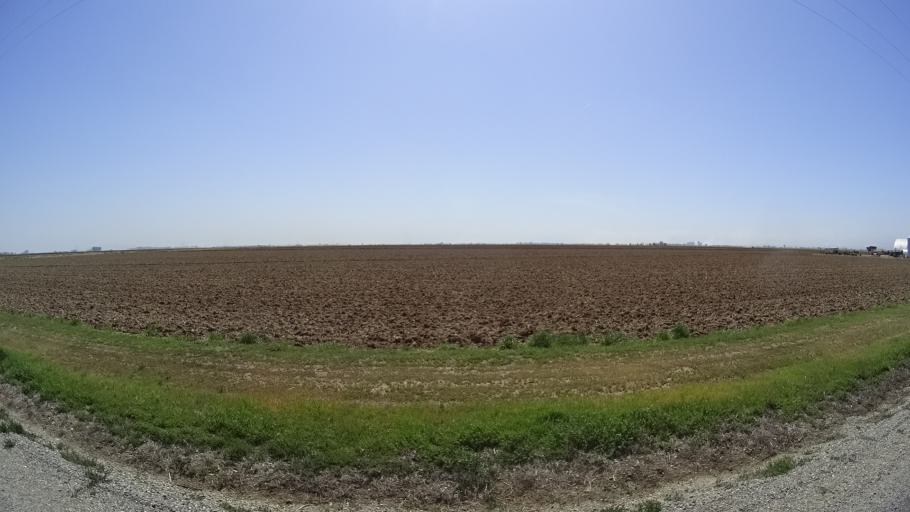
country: US
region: California
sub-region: Glenn County
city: Willows
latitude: 39.4945
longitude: -122.1667
